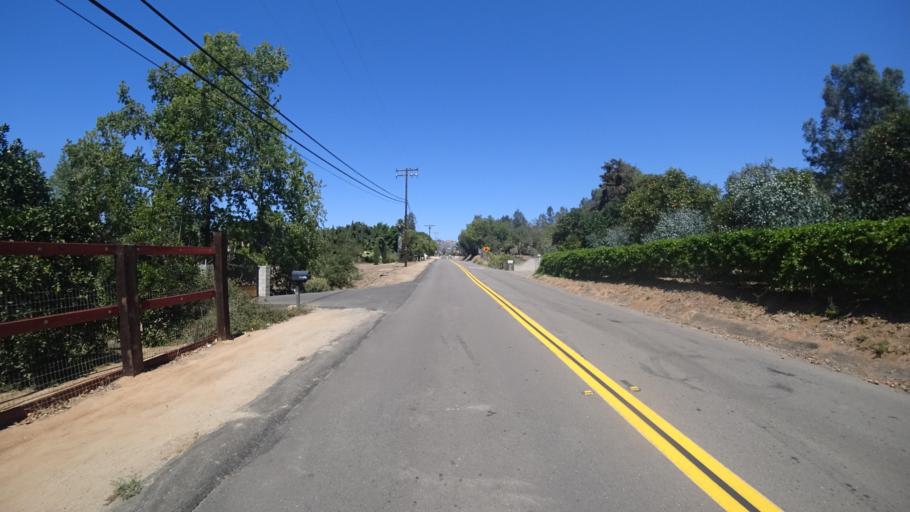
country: US
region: California
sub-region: San Diego County
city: Rainbow
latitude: 33.4074
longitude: -117.1455
